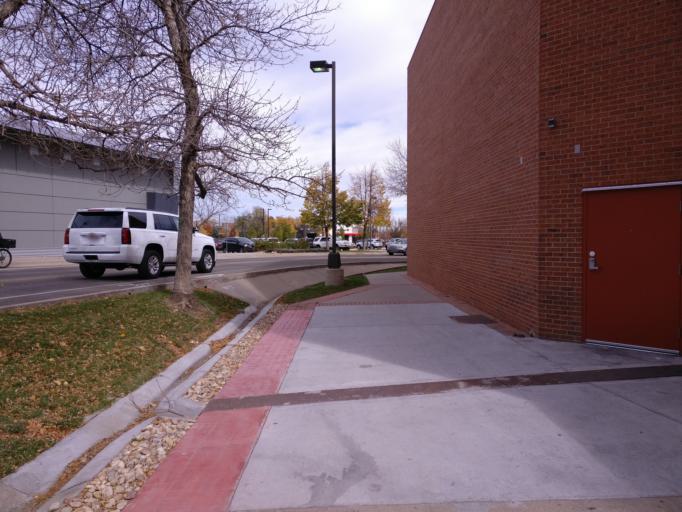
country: US
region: Colorado
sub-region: Boulder County
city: Boulder
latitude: 40.0203
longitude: -105.2600
